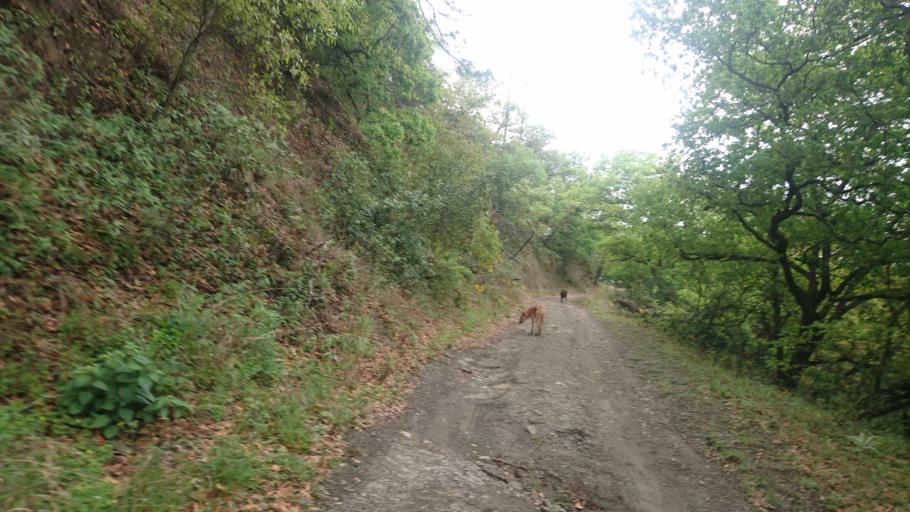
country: MX
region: Nuevo Leon
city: Garza Garcia
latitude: 25.6058
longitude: -100.3414
